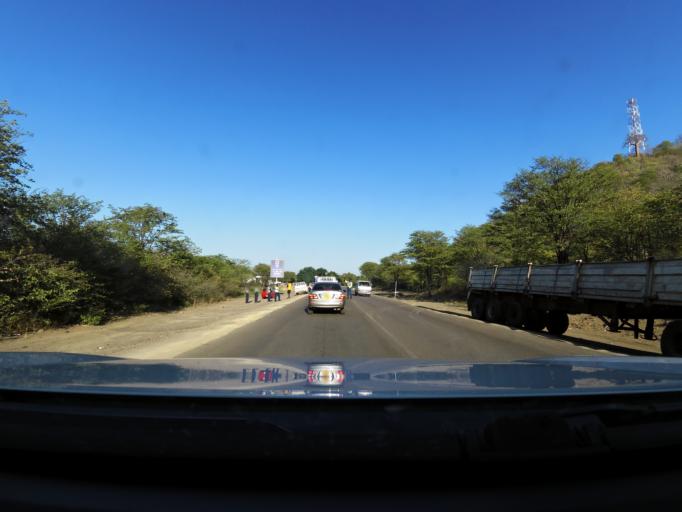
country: ZW
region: Matabeleland North
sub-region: Hwange District
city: Hwange
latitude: -18.3464
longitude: 26.5057
